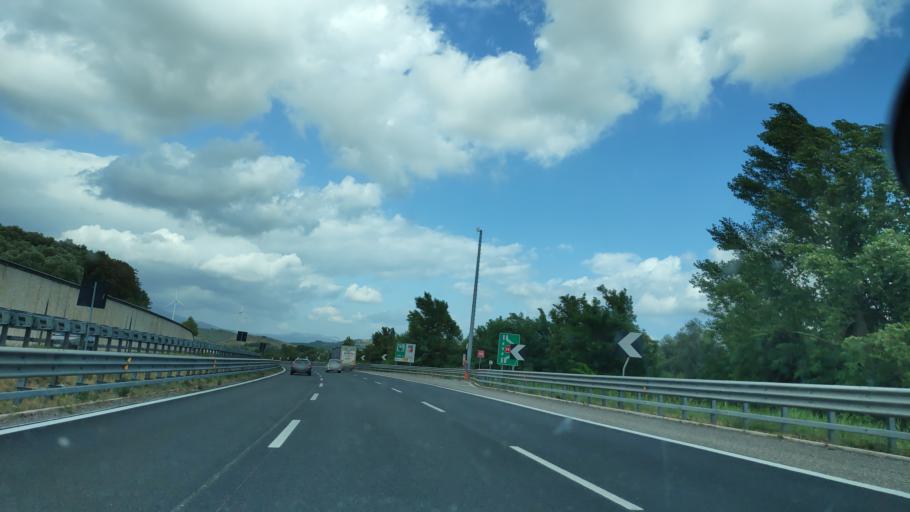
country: IT
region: Campania
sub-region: Provincia di Salerno
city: Quadrivio
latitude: 40.6134
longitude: 15.1490
